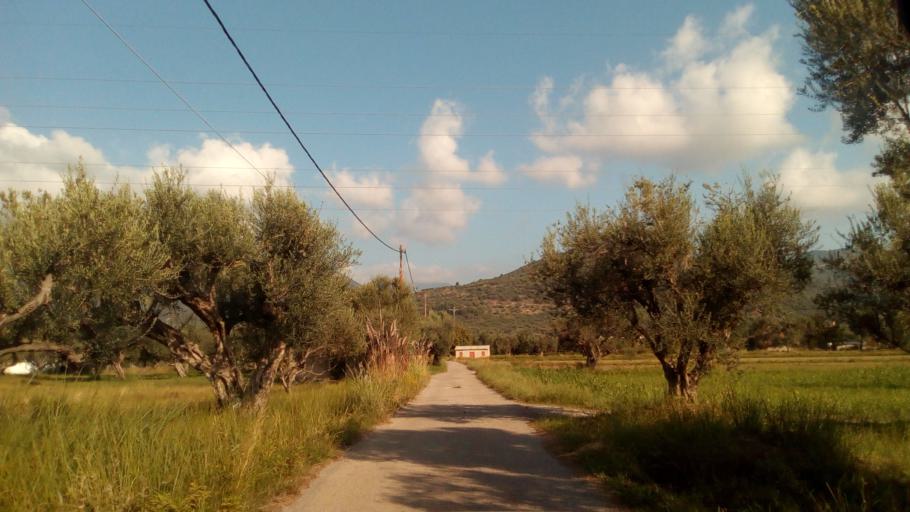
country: GR
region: West Greece
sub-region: Nomos Aitolias kai Akarnanias
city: Nafpaktos
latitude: 38.4113
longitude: 21.8893
